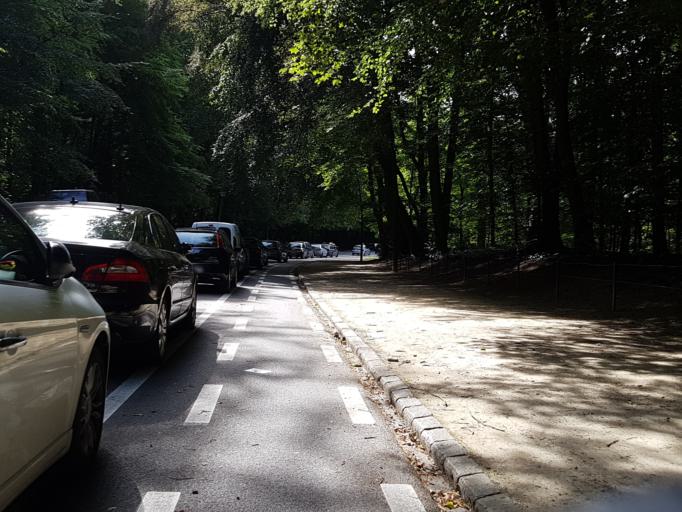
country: BE
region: Brussels Capital
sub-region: Bruxelles-Capitale
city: Brussels
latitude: 50.8089
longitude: 4.3798
